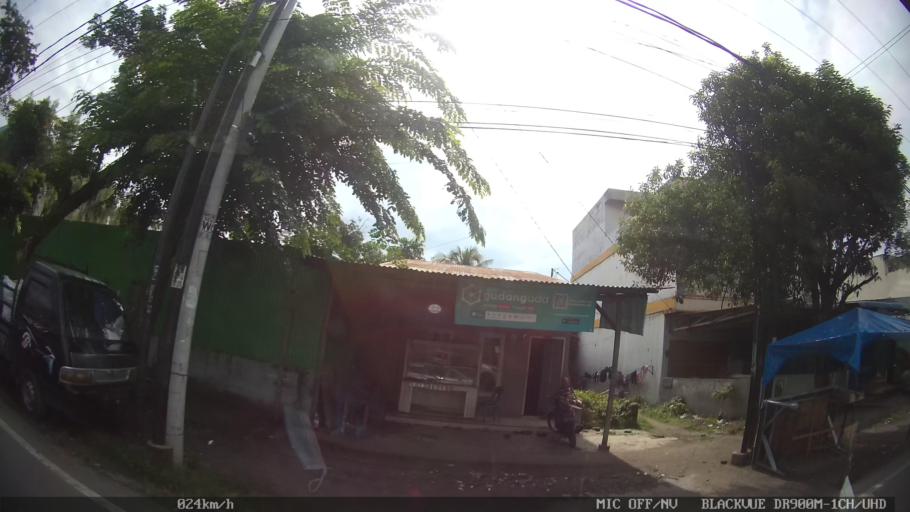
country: ID
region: North Sumatra
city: Sunggal
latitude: 3.6064
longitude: 98.6083
